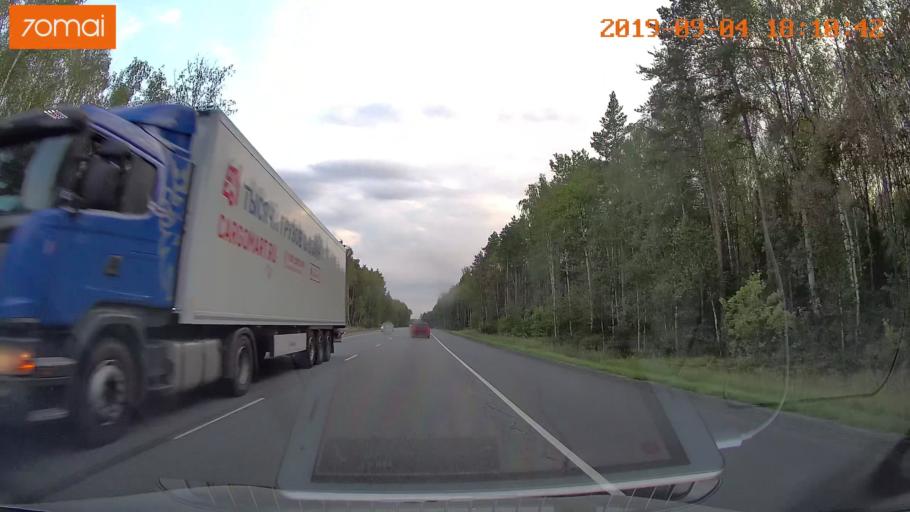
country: RU
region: Moskovskaya
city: Lopatinskiy
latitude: 55.3851
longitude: 38.7624
